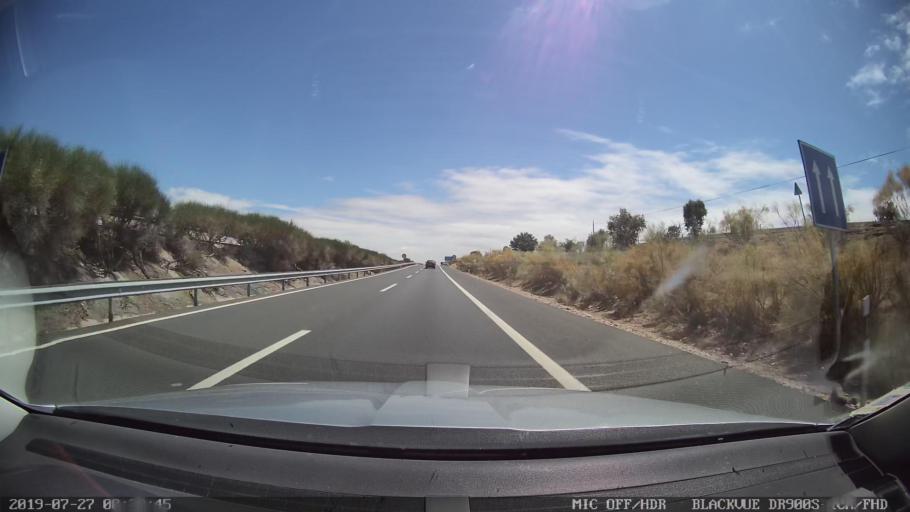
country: ES
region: Extremadura
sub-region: Provincia de Caceres
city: Peraleda de la Mata
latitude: 39.8904
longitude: -5.4246
